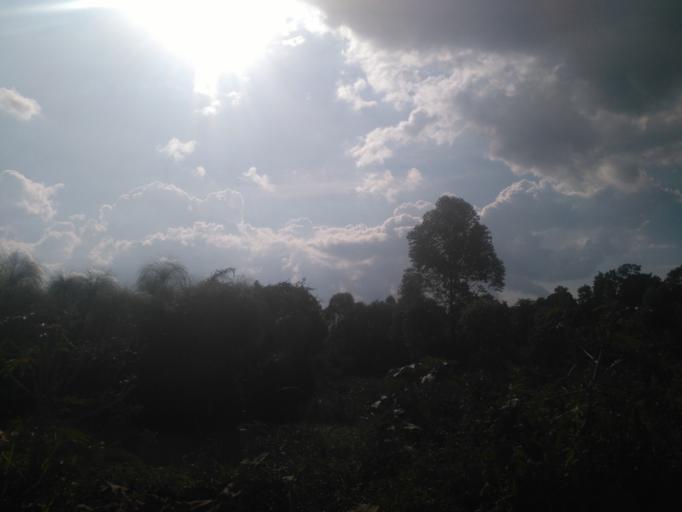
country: UG
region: Central Region
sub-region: Wakiso District
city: Wakiso
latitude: 0.3134
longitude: 32.4430
